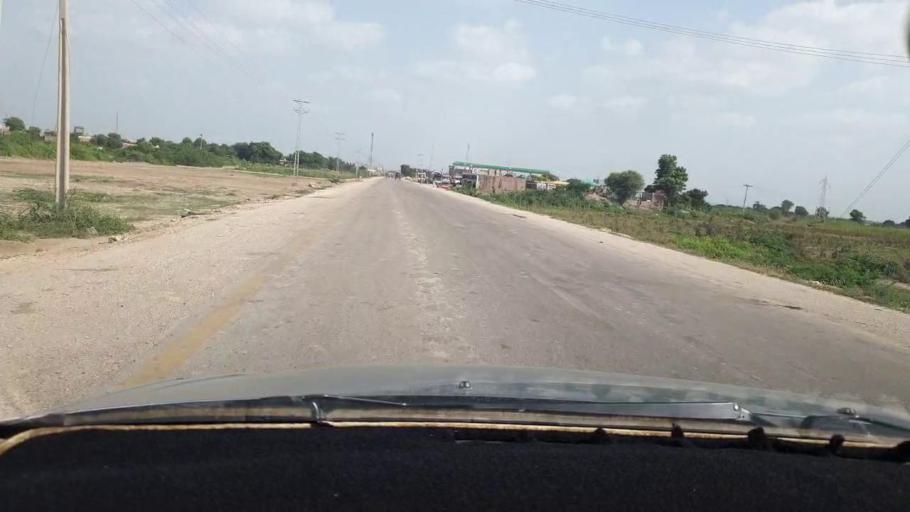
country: PK
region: Sindh
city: Naukot
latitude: 24.8610
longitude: 69.3919
